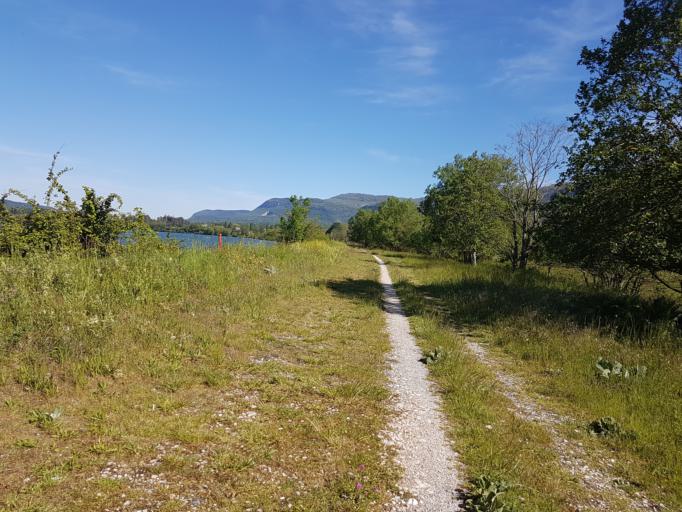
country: FR
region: Rhone-Alpes
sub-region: Departement de l'Ain
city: Villebois
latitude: 45.8299
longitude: 5.4377
